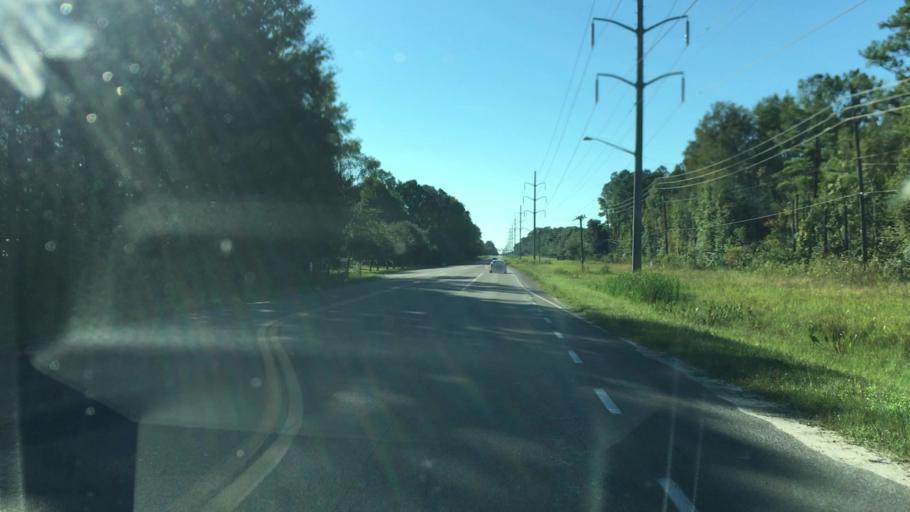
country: US
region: Florida
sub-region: Alachua County
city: Gainesville
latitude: 29.7032
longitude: -82.3338
